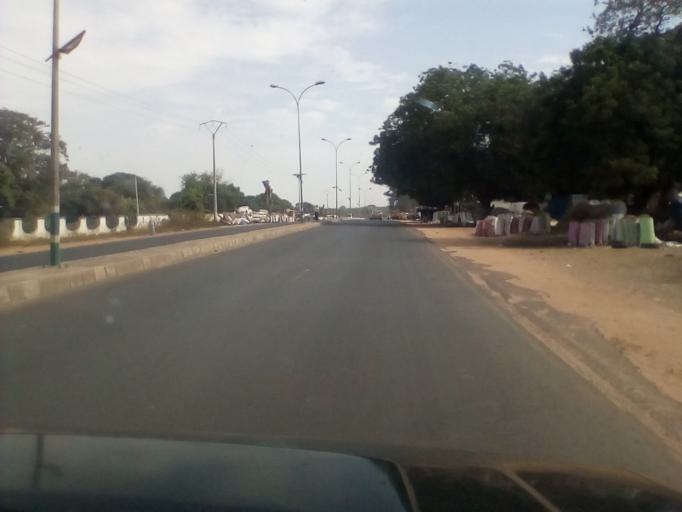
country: GM
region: Western
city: Abuko
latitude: 13.4005
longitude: -16.6525
